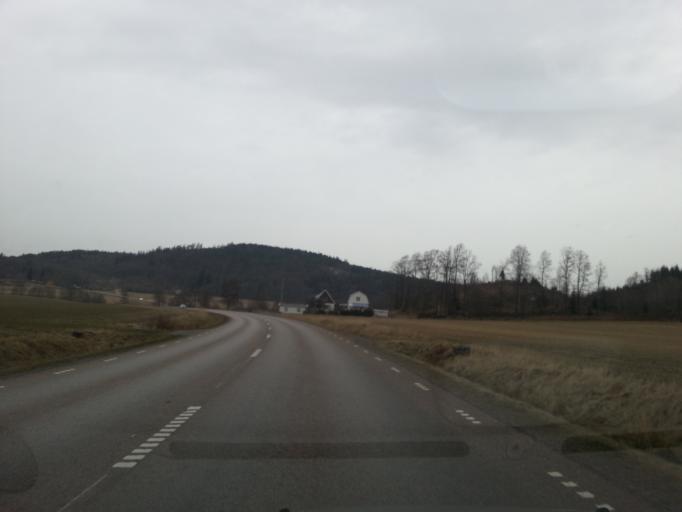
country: SE
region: Vaestra Goetaland
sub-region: Lilla Edets Kommun
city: Lilla Edet
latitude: 58.1396
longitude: 12.0988
